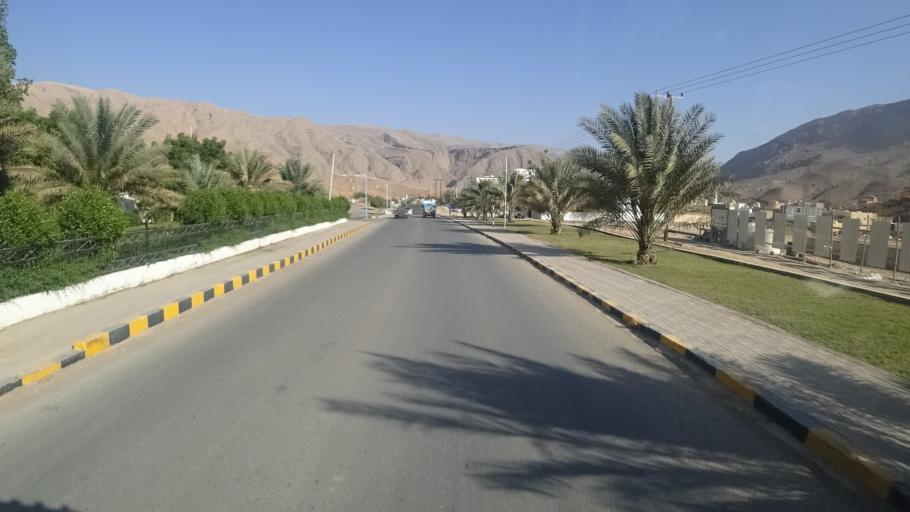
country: OM
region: Ash Sharqiyah
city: Badiyah
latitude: 22.5800
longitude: 59.0923
